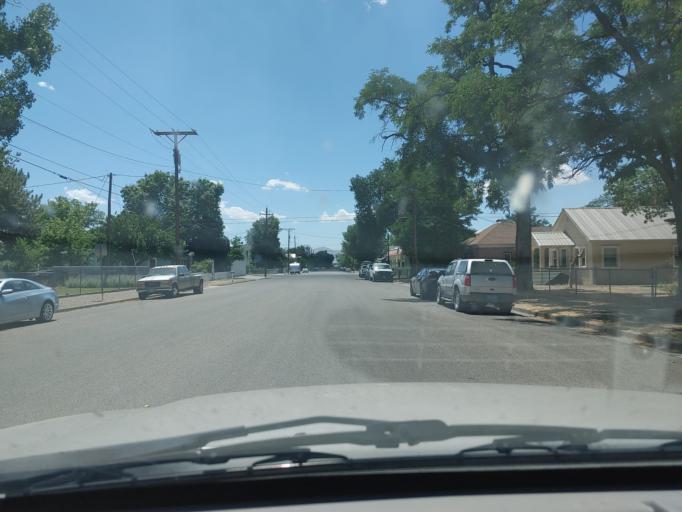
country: US
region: Nevada
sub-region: Humboldt County
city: Winnemucca
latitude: 40.9728
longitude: -117.7378
